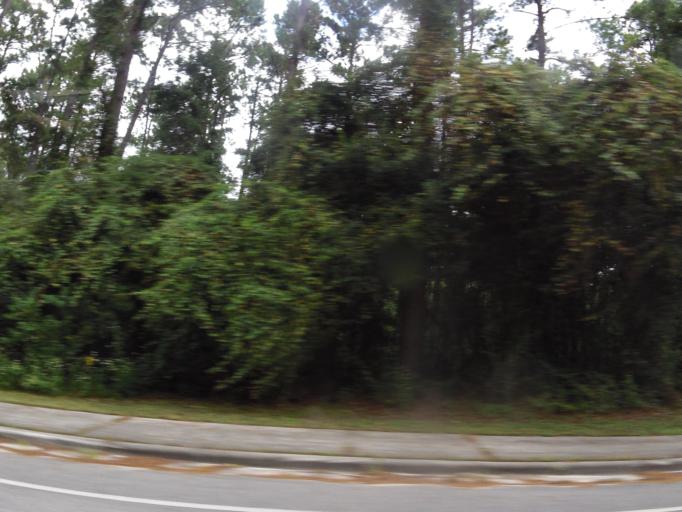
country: US
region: Florida
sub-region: Clay County
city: Lakeside
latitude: 30.1057
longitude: -81.7952
